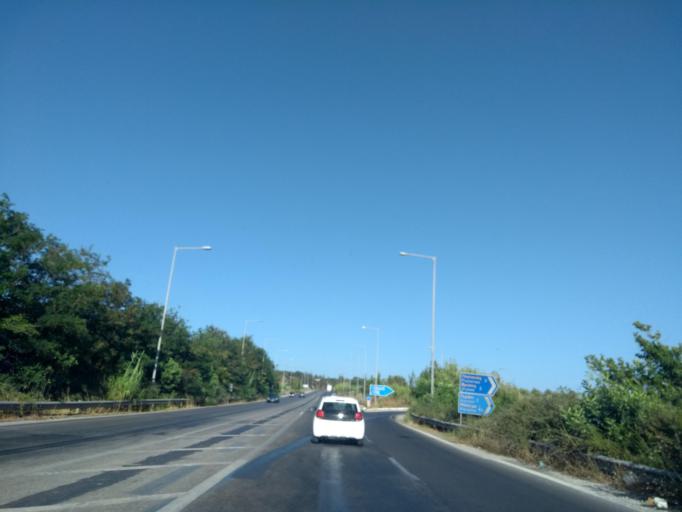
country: GR
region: Crete
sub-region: Nomos Chanias
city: Gerani
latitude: 35.5121
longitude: 23.8939
